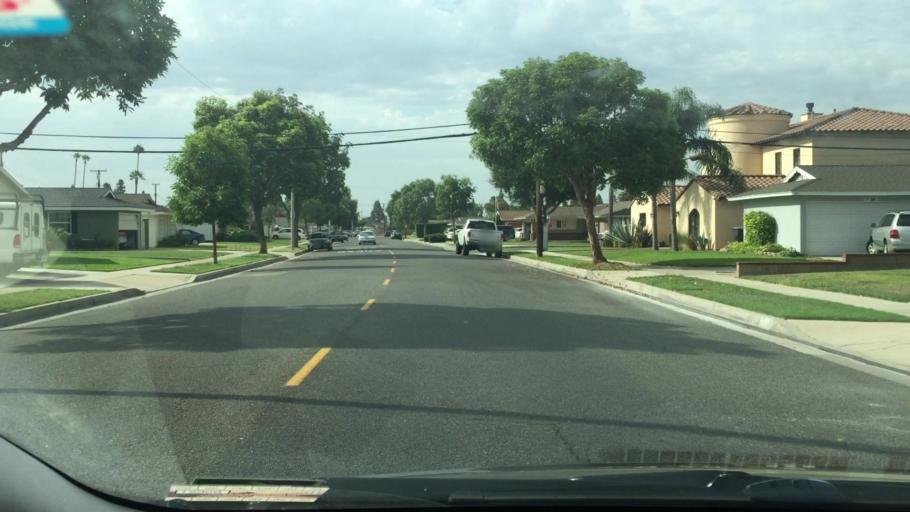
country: US
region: California
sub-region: Orange County
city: Cypress
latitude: 33.7882
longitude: -118.0358
